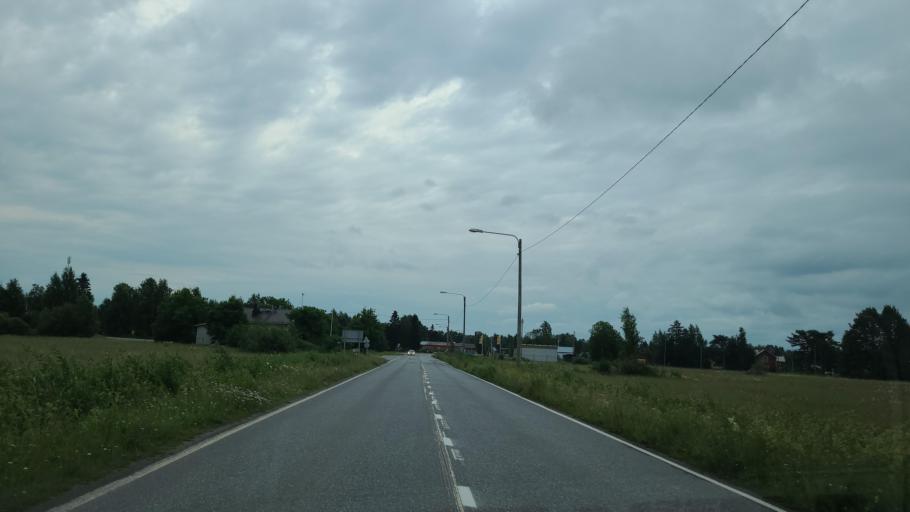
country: FI
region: Ostrobothnia
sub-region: Vaasa
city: Replot
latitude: 63.2340
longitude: 21.4044
